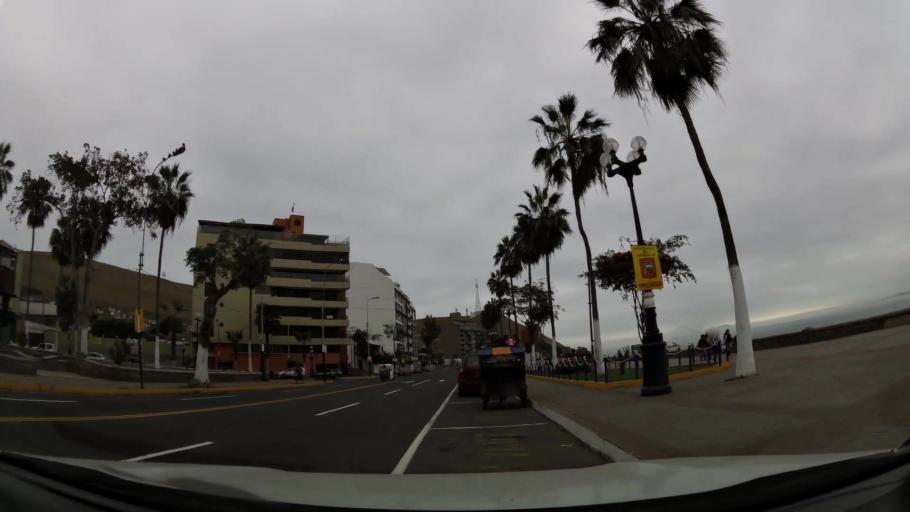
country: PE
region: Lima
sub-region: Lima
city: Surco
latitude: -12.1674
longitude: -77.0300
